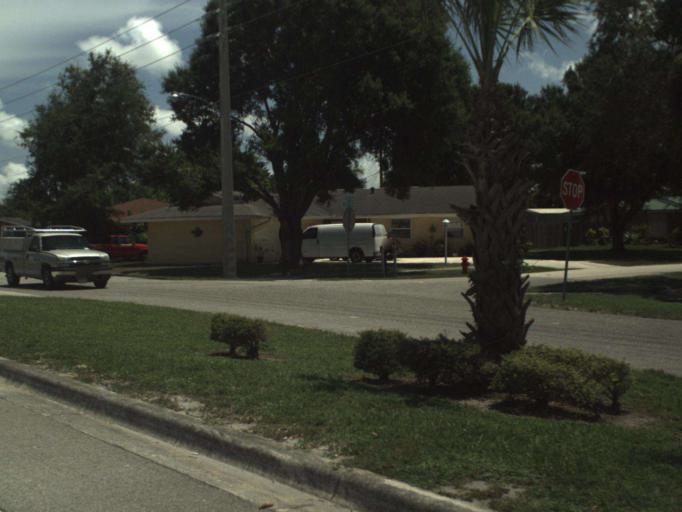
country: US
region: Florida
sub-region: Saint Lucie County
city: River Park
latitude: 27.3258
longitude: -80.3205
